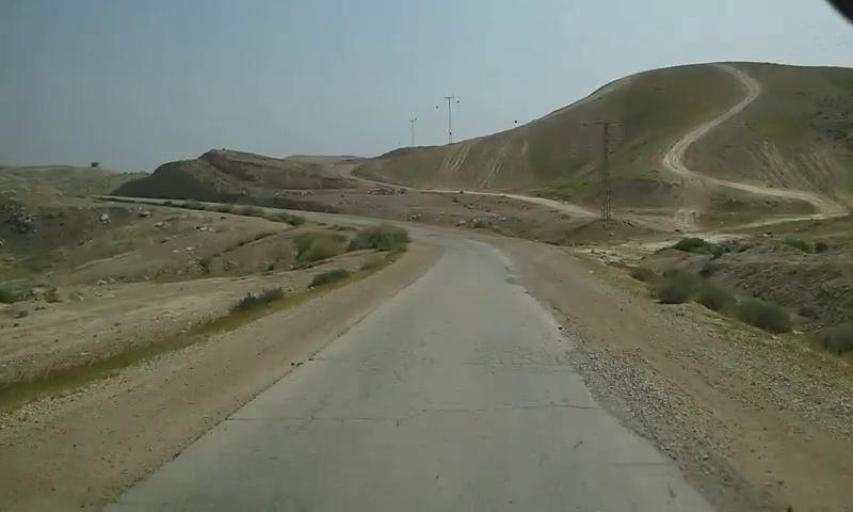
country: PS
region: West Bank
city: Jericho
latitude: 31.7900
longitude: 35.4288
